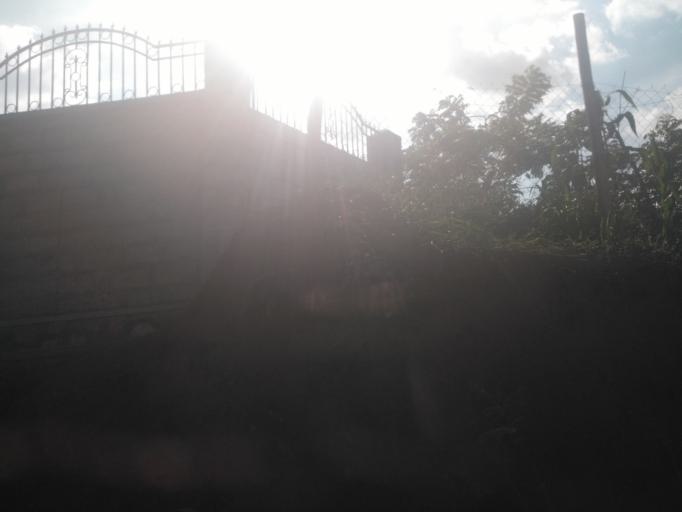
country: UG
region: Central Region
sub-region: Wakiso District
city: Wakiso
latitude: 0.2944
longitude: 32.4526
